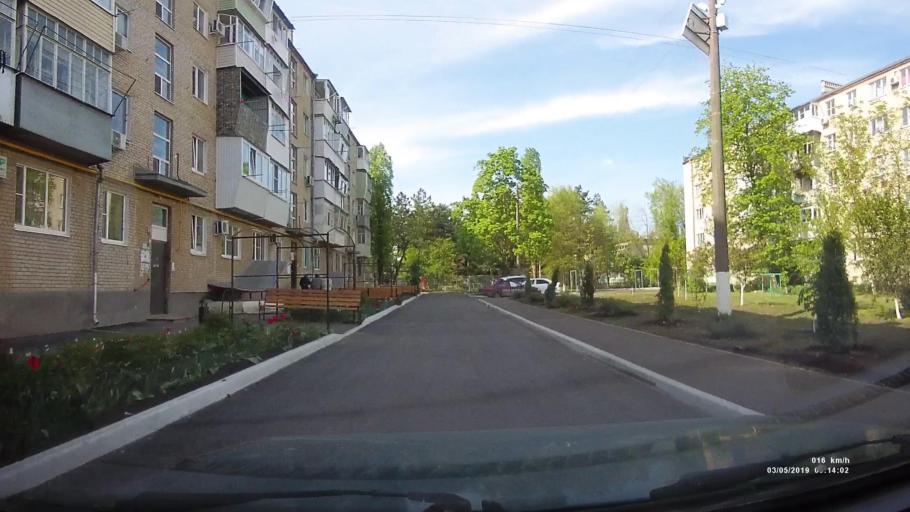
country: RU
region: Rostov
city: Azov
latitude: 47.0987
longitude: 39.4242
